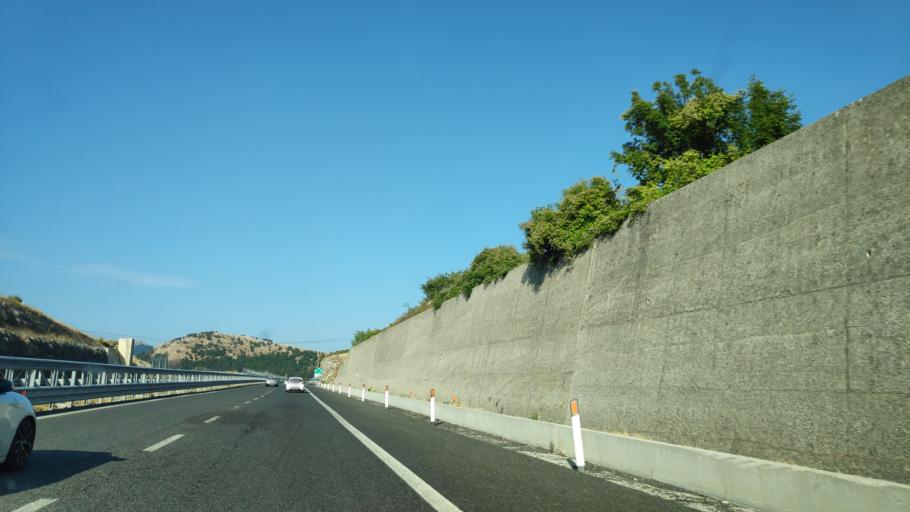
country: IT
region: Calabria
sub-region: Provincia di Cosenza
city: Morano Calabro
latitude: 39.8693
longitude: 16.1169
